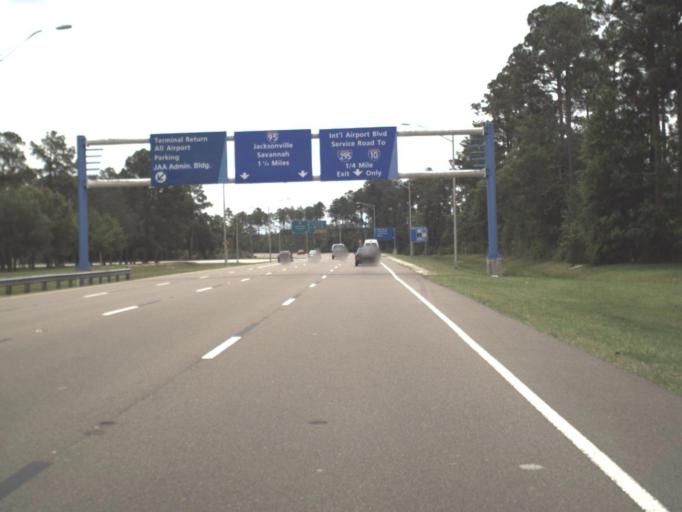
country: US
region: Florida
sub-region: Nassau County
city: Nassau Village-Ratliff
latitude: 30.4875
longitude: -81.6734
